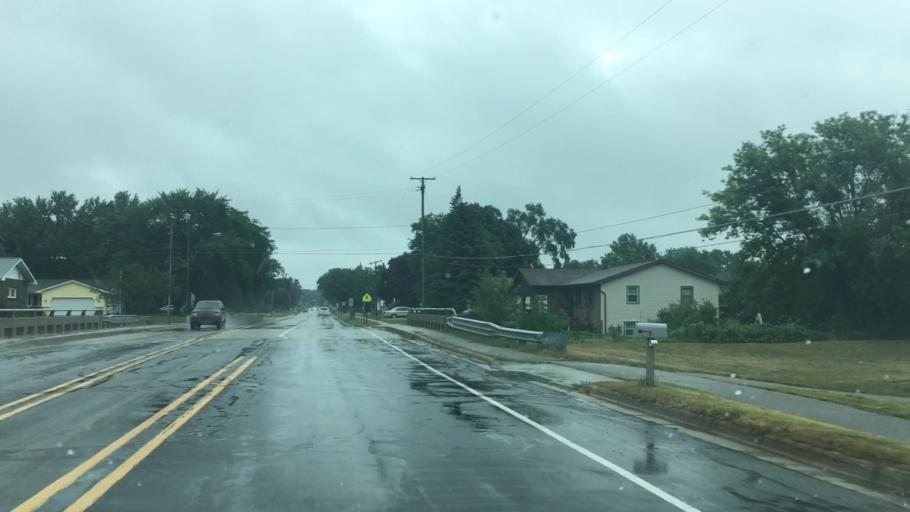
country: US
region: Michigan
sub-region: Ottawa County
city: Hudsonville
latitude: 42.8805
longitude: -85.8553
